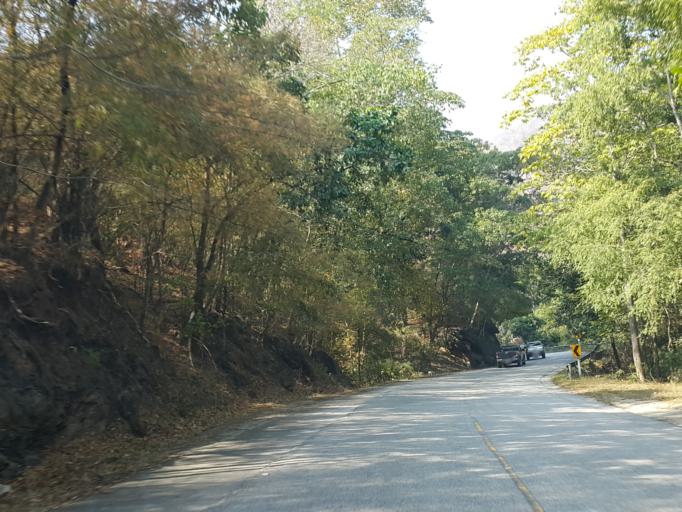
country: TH
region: Chiang Mai
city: Hot
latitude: 18.2349
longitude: 98.5342
